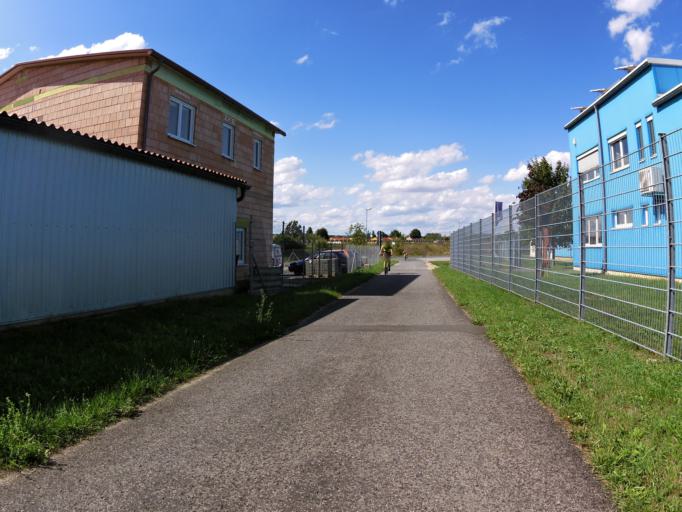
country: DE
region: Bavaria
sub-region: Regierungsbezirk Unterfranken
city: Marktsteft
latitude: 49.6889
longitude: 10.1448
